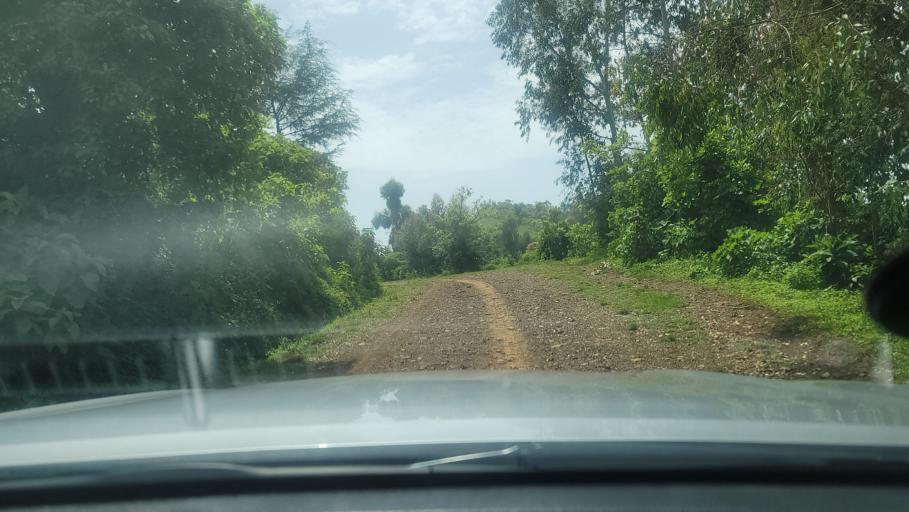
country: ET
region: Oromiya
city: Agaro
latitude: 7.8360
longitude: 36.4063
